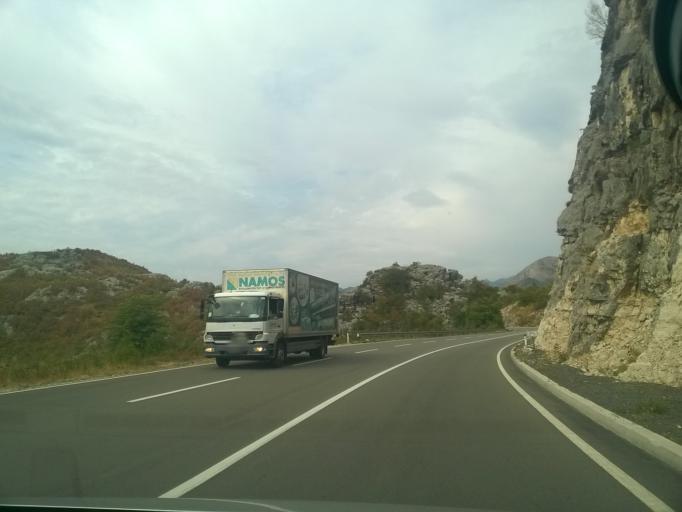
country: ME
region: Cetinje
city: Cetinje
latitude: 42.3816
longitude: 19.0118
